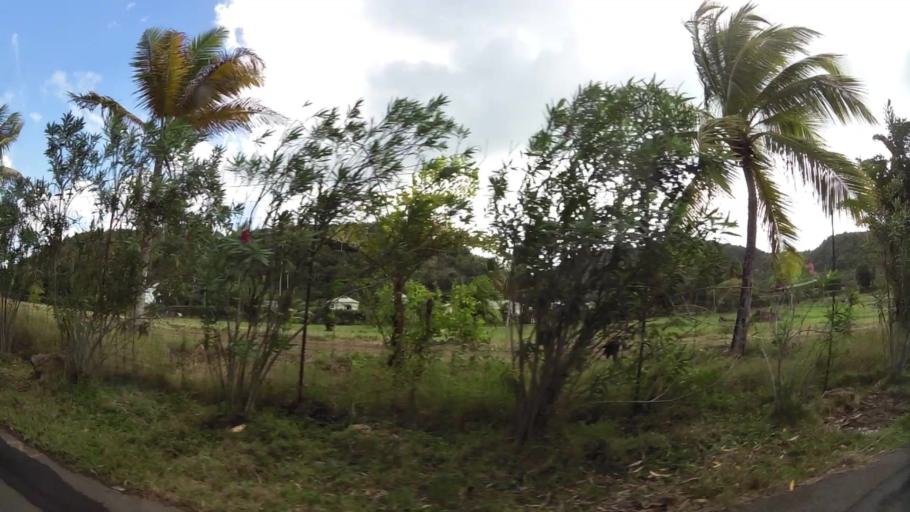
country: AG
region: Saint John
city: Saint John's
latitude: 17.1195
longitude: -61.8886
